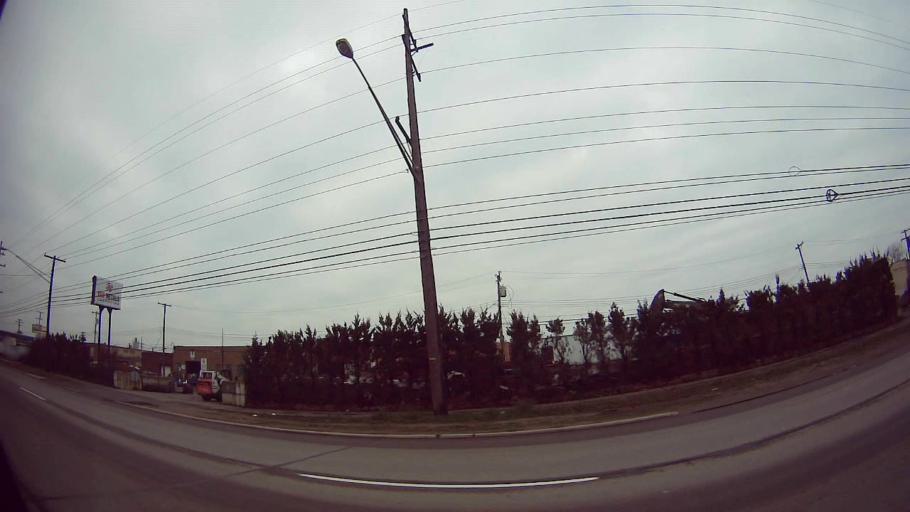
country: US
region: Michigan
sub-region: Wayne County
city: Redford
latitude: 42.3747
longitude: -83.2757
